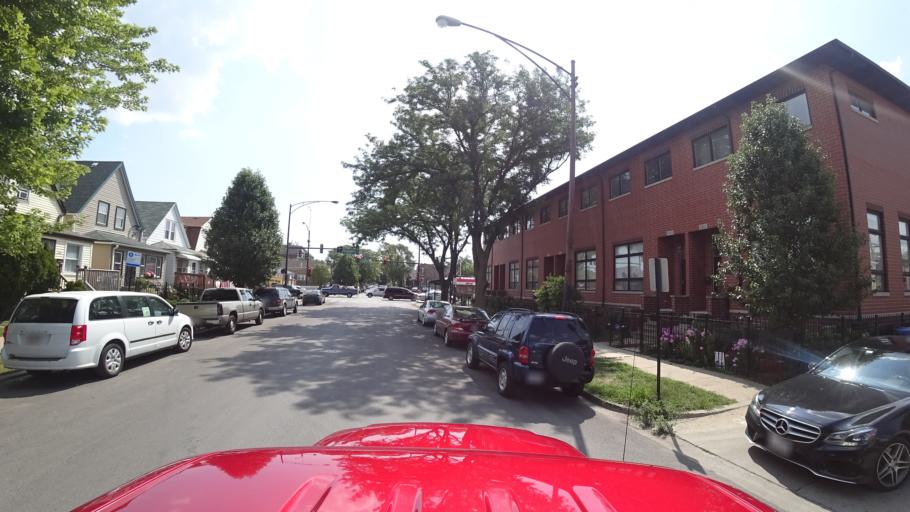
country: US
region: Illinois
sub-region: Cook County
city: Chicago
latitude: 41.8283
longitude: -87.6954
